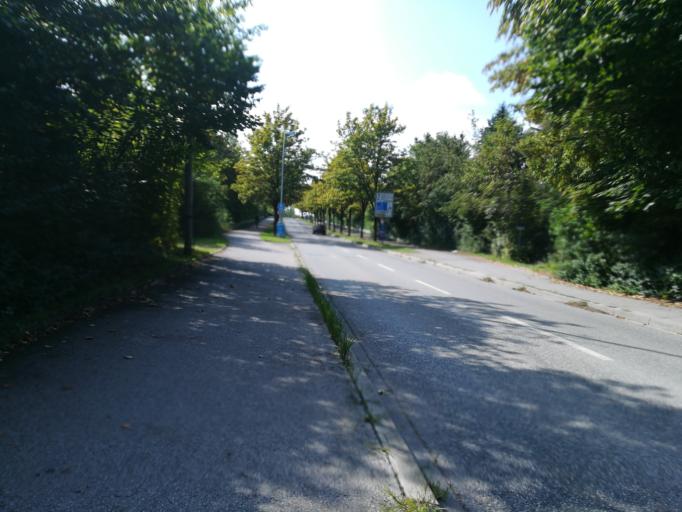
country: DE
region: Bavaria
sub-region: Upper Bavaria
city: Karlsfeld
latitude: 48.1936
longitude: 11.5231
